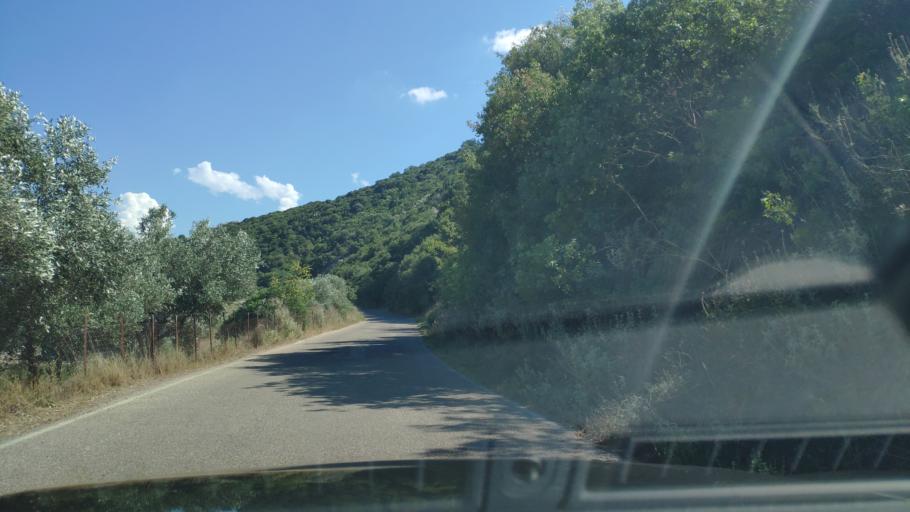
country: GR
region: West Greece
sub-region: Nomos Aitolias kai Akarnanias
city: Katouna
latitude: 38.8277
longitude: 21.0995
